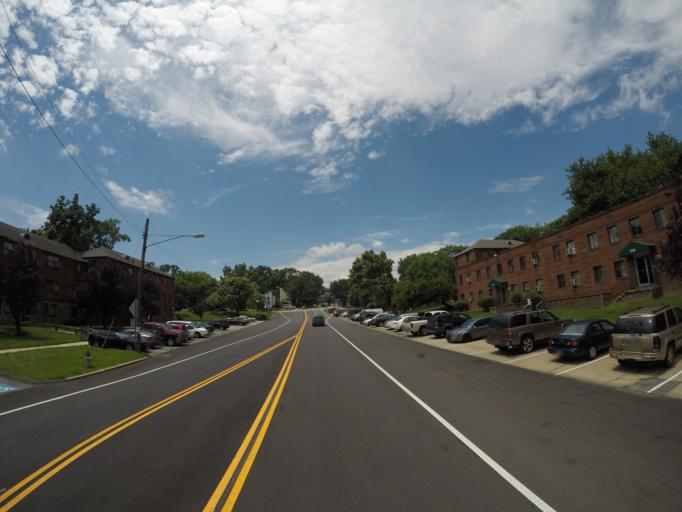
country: US
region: Maryland
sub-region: Prince George's County
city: Chillum
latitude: 38.9651
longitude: -76.9999
